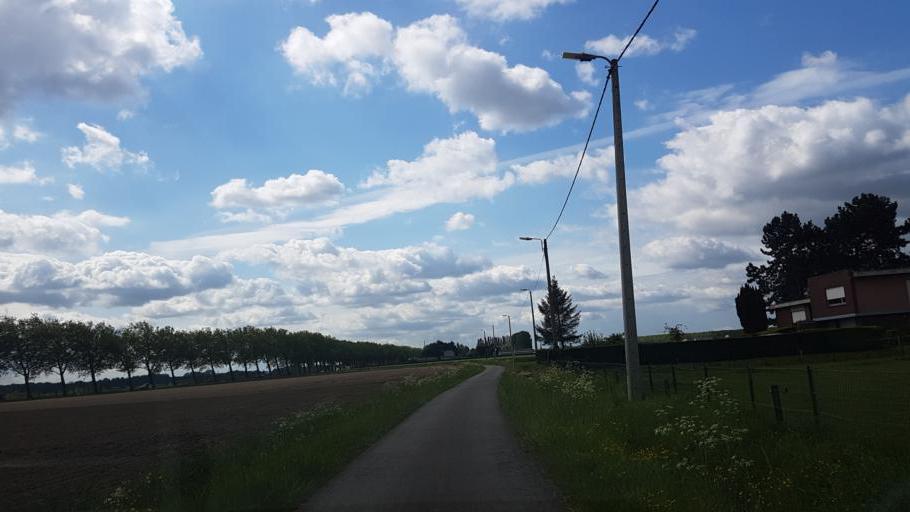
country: BE
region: Flanders
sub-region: Provincie Vlaams-Brabant
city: Steenokkerzeel
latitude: 50.9458
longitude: 4.4924
